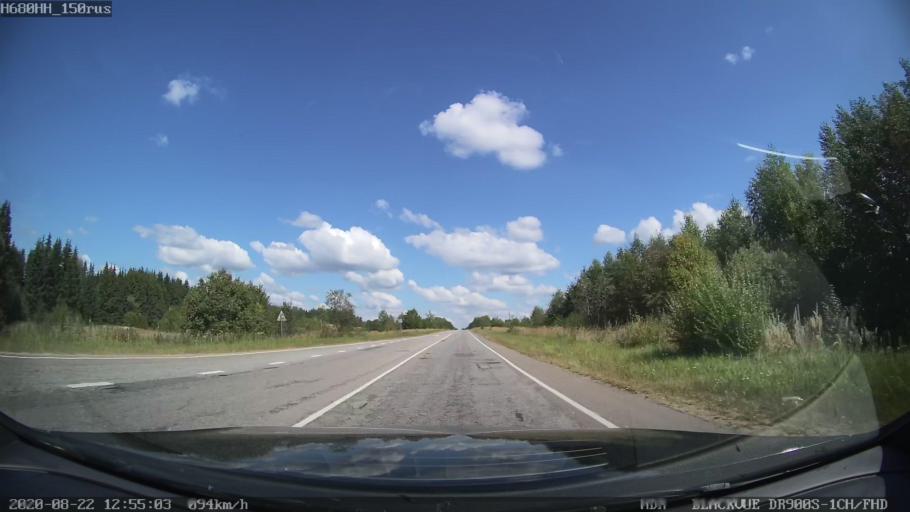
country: RU
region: Tverskaya
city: Rameshki
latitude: 57.5393
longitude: 36.2935
